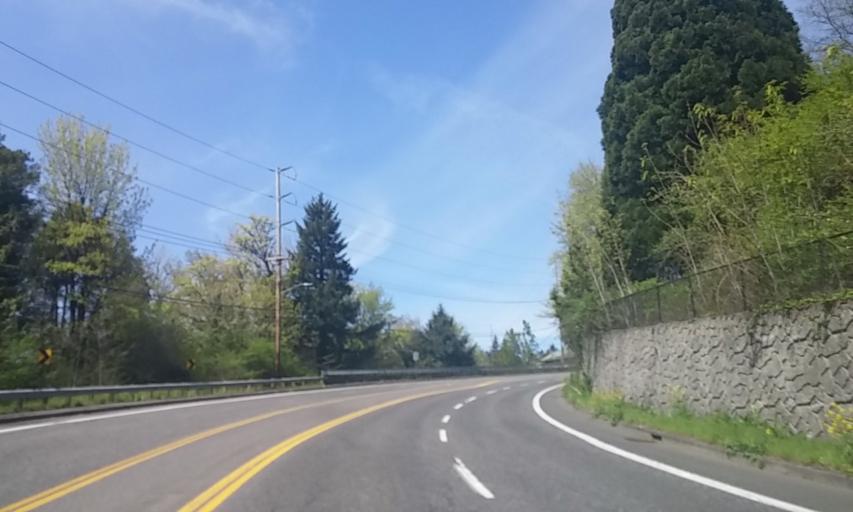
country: US
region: Oregon
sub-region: Washington County
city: West Slope
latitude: 45.5061
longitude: -122.7372
